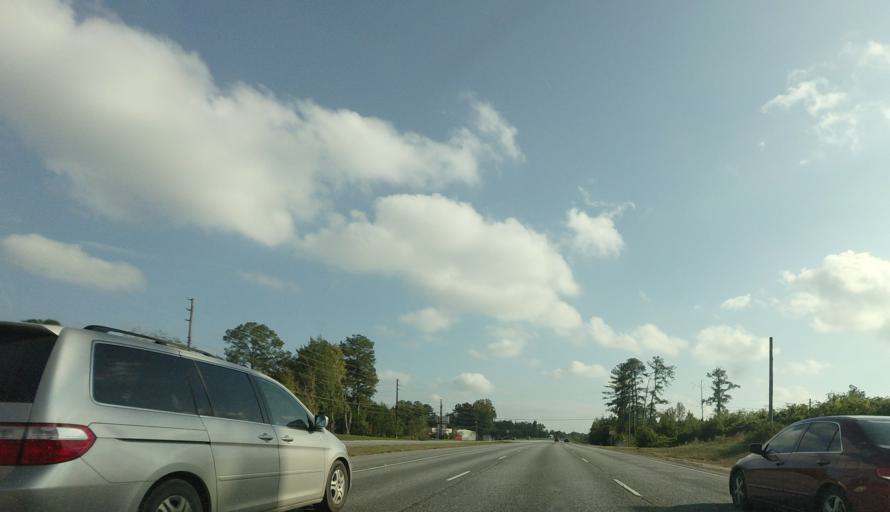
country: US
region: Georgia
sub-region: Bibb County
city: Macon
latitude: 32.7532
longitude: -83.6594
